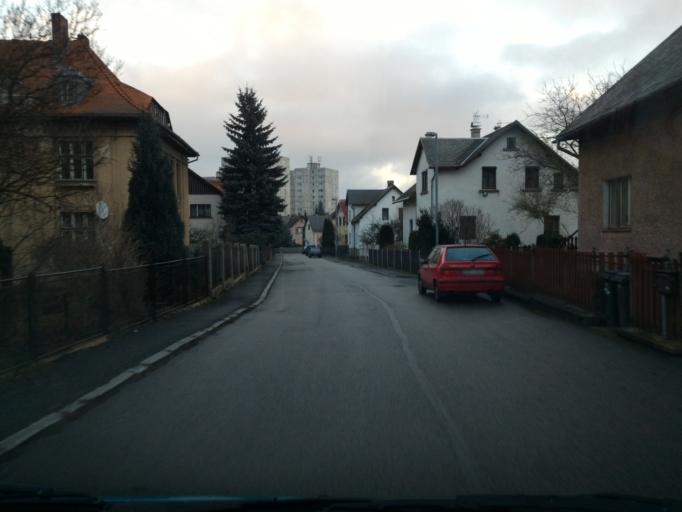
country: CZ
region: Ustecky
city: Varnsdorf
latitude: 50.9049
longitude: 14.6209
